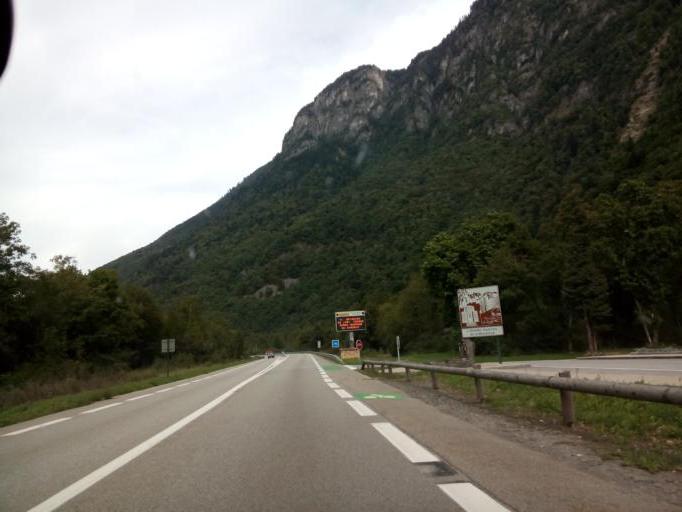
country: FR
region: Rhone-Alpes
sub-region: Departement de l'Isere
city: Vaulnaveys-le-Bas
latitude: 45.0545
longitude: 5.8548
